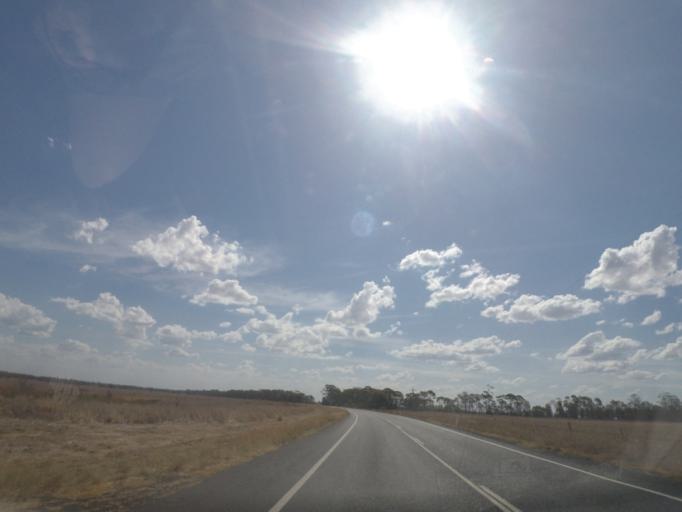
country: AU
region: Queensland
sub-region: Southern Downs
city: Stanthorpe
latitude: -28.4037
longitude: 151.1812
